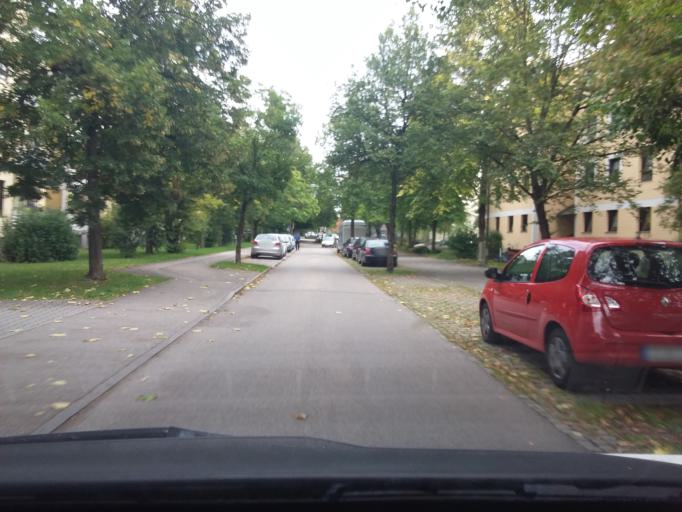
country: DE
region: Bavaria
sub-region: Upper Bavaria
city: Oberschleissheim
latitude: 48.2538
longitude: 11.5505
